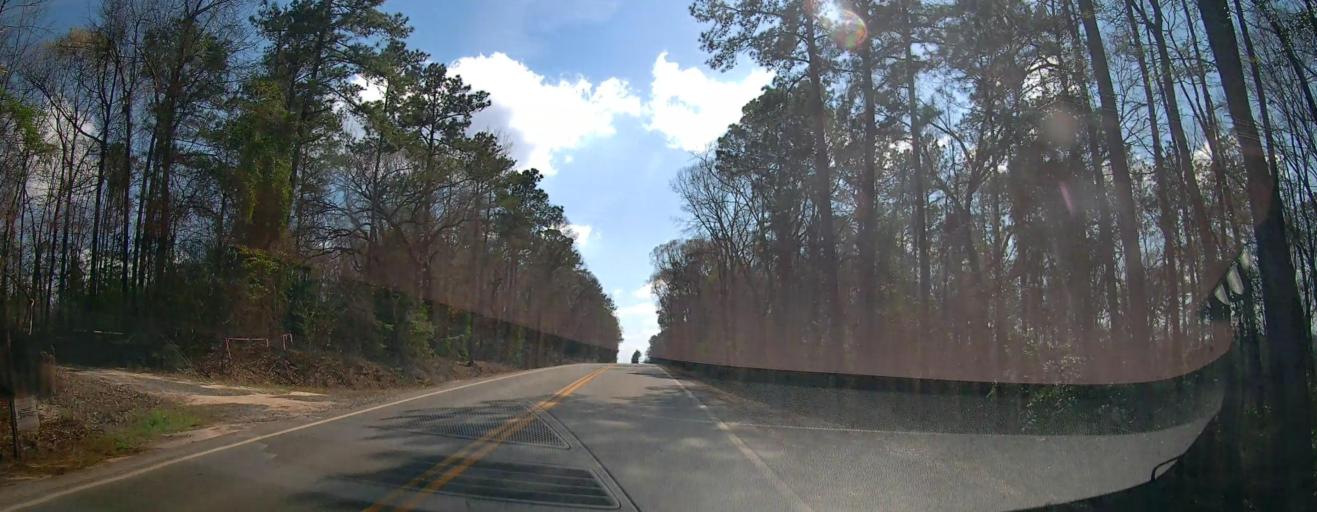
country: US
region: Georgia
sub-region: Wilkinson County
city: Gordon
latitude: 32.8085
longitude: -83.3250
